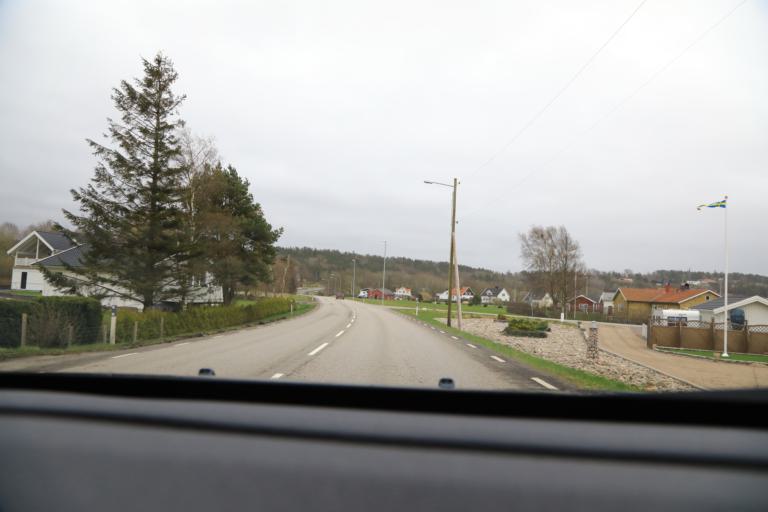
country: SE
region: Halland
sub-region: Kungsbacka Kommun
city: Frillesas
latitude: 57.3146
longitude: 12.1776
